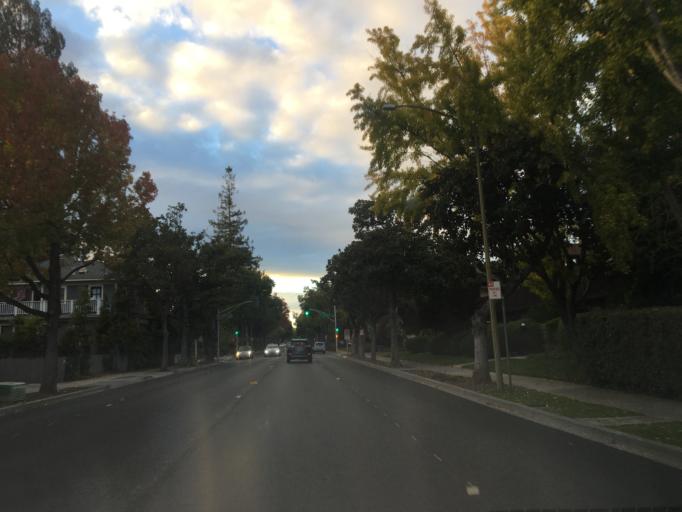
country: US
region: California
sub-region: Santa Clara County
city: Palo Alto
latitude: 37.4479
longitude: -122.1523
